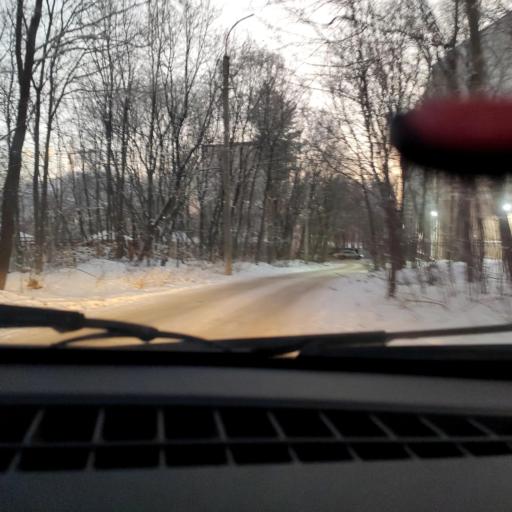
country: RU
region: Bashkortostan
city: Ufa
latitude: 54.7546
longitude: 55.9832
